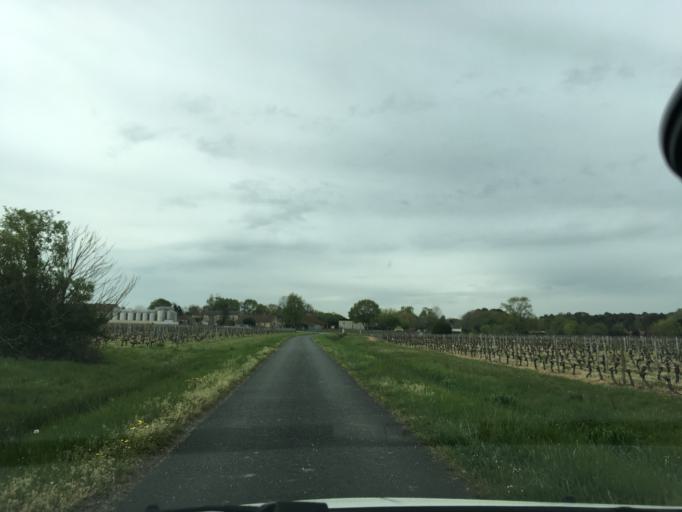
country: FR
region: Aquitaine
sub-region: Departement de la Gironde
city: Lesparre-Medoc
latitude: 45.3162
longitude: -0.8950
